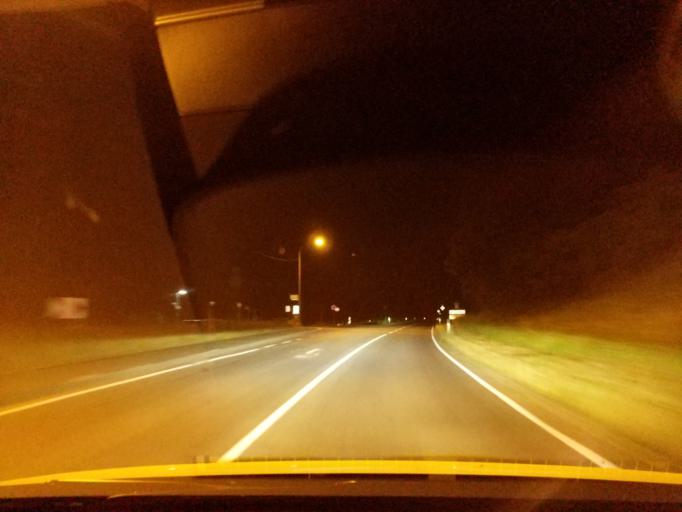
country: DE
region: Rheinland-Pfalz
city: Katzweiler
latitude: 49.5071
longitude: 7.6884
